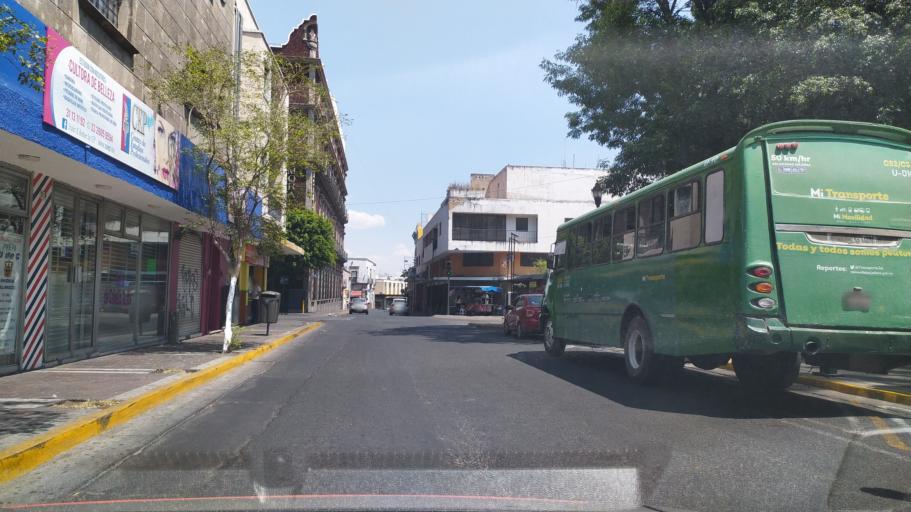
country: MX
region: Jalisco
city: Guadalajara
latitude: 20.6729
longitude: -103.3468
